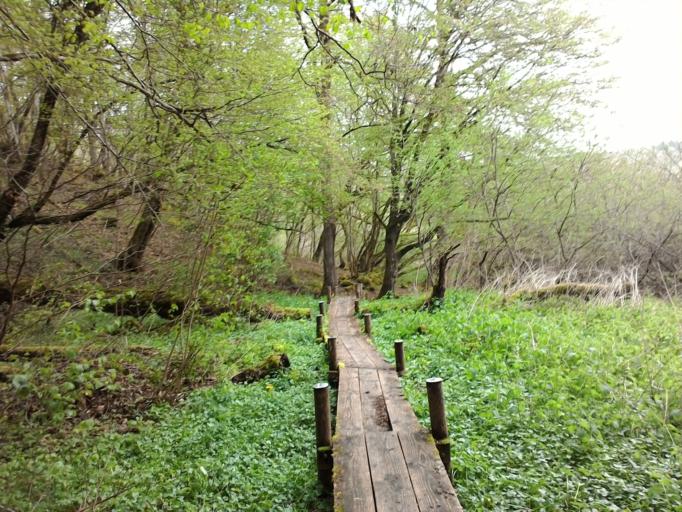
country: FR
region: Bourgogne
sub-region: Departement de la Cote-d'Or
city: Saulieu
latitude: 47.2510
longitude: 4.1829
